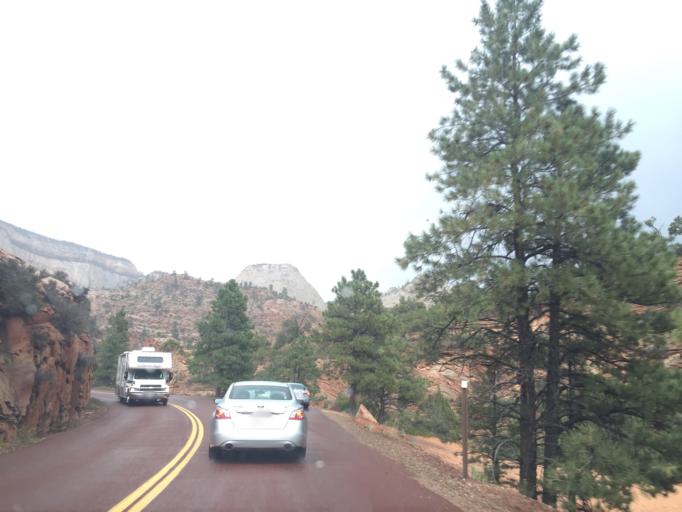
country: US
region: Utah
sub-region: Washington County
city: Hildale
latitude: 37.2193
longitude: -112.9173
